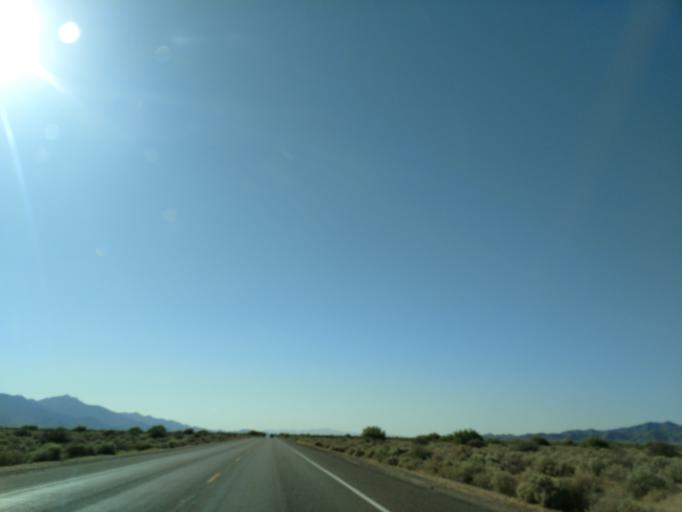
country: US
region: Arizona
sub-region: Maricopa County
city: Laveen
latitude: 33.2281
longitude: -112.0848
